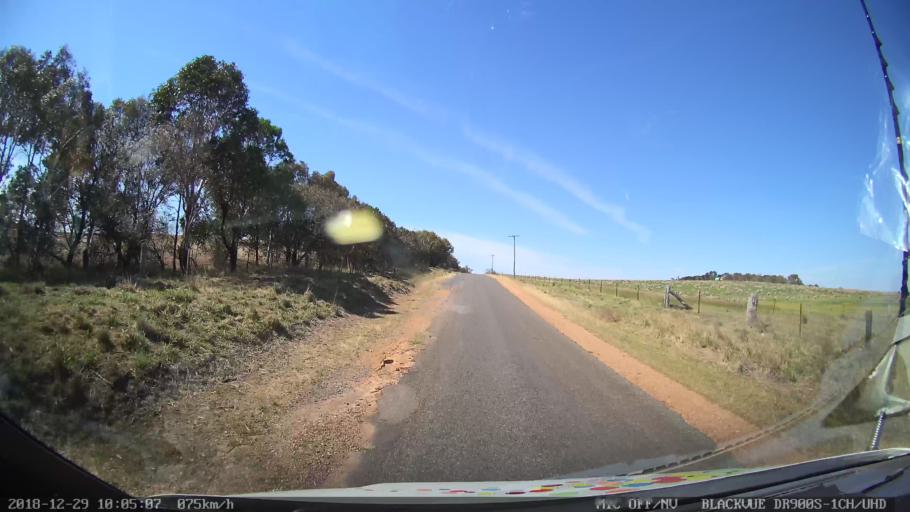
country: AU
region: New South Wales
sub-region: Goulburn Mulwaree
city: Goulburn
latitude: -34.8297
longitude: 149.4537
